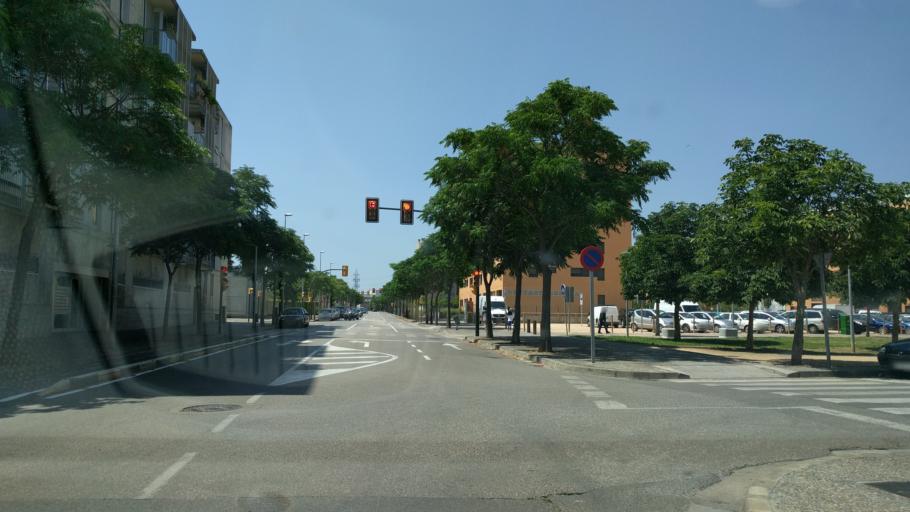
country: ES
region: Catalonia
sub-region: Provincia de Girona
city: Salt
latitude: 41.9729
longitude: 2.8046
